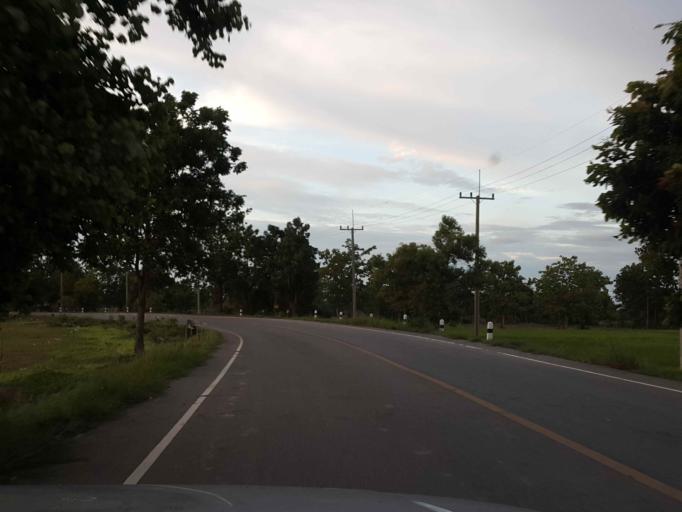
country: TH
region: Sukhothai
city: Ban Dan Lan Hoi
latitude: 17.1145
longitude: 99.5961
